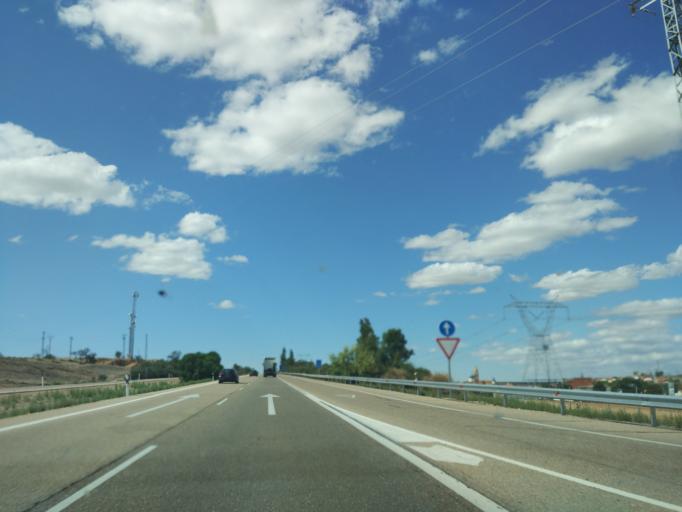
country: ES
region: Castille and Leon
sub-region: Provincia de Valladolid
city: Rueda
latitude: 41.4038
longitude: -4.9611
